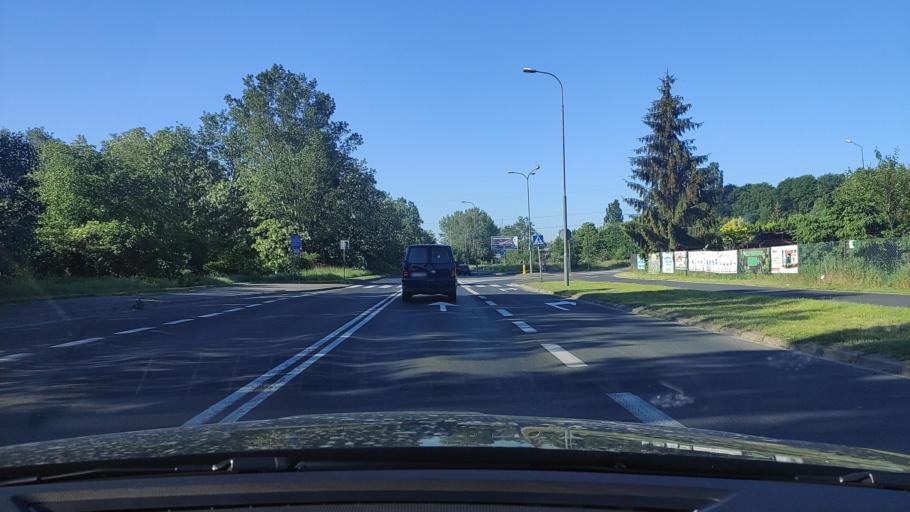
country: PL
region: Greater Poland Voivodeship
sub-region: Poznan
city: Poznan
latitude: 52.3769
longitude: 16.9192
